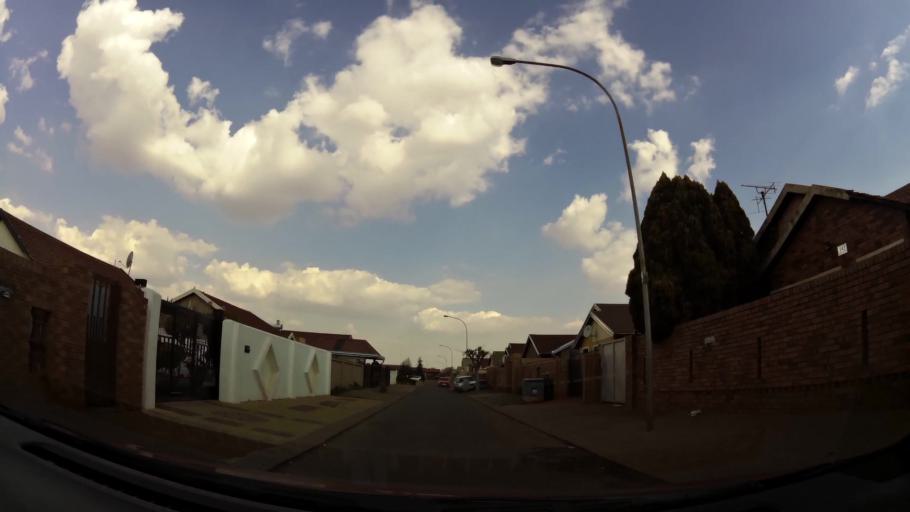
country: ZA
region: Gauteng
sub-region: City of Johannesburg Metropolitan Municipality
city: Roodepoort
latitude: -26.2116
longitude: 27.8662
